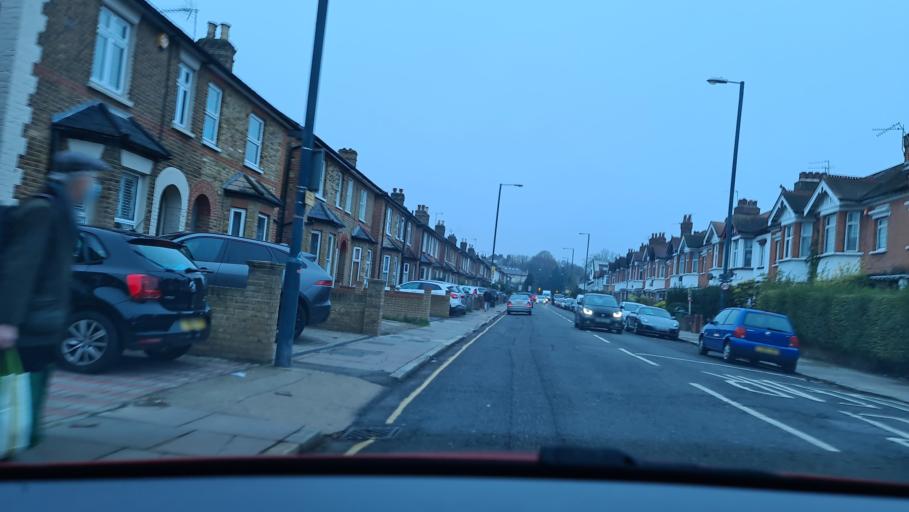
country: GB
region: England
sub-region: Greater London
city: Richmond
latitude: 51.4643
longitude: -0.2884
